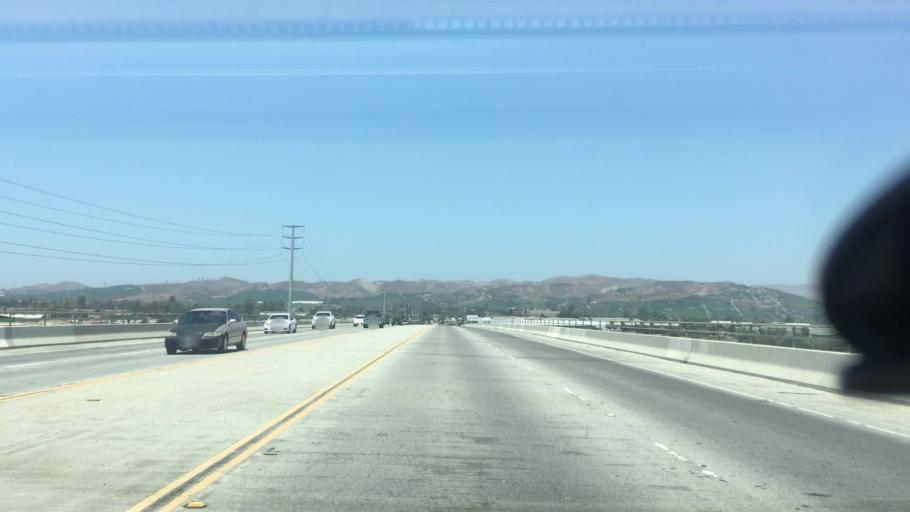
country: US
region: California
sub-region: Ventura County
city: Saticoy
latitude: 34.2761
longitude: -119.1380
